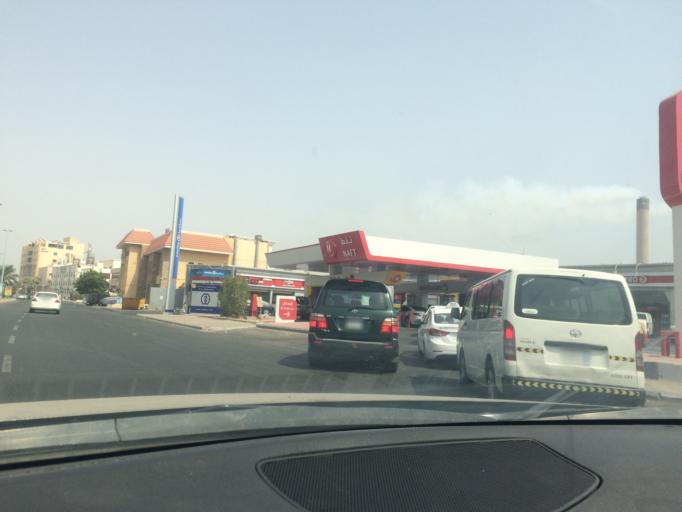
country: SA
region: Makkah
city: Jeddah
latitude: 21.5589
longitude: 39.1156
